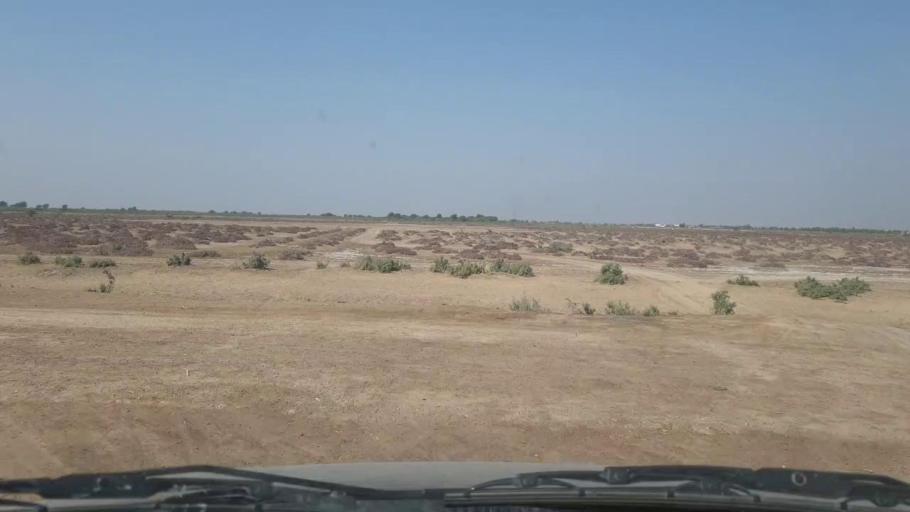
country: PK
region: Sindh
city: Samaro
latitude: 25.2648
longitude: 69.3416
